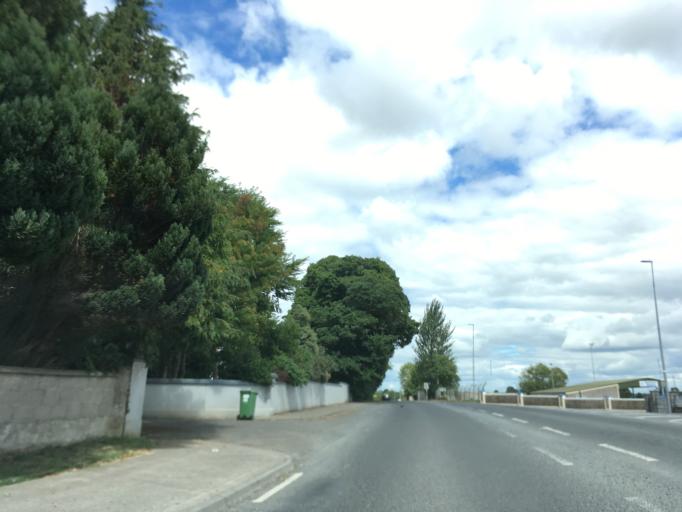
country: IE
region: Munster
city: Cashel
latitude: 52.4424
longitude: -7.8822
